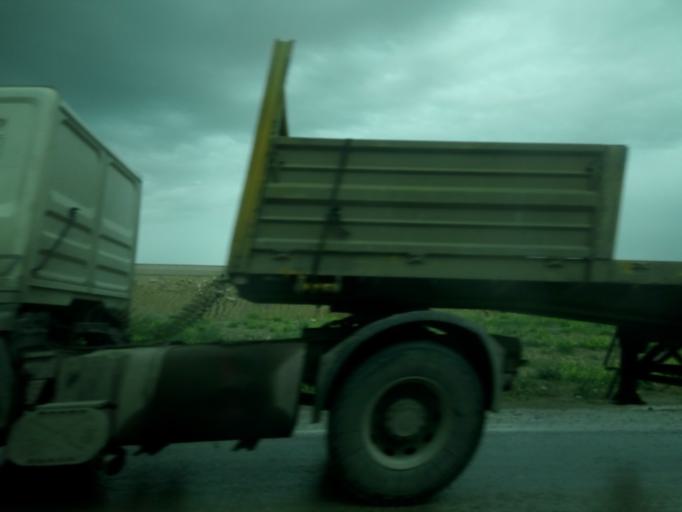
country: DZ
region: Medea
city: Ksar el Boukhari
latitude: 35.8818
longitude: 2.7353
